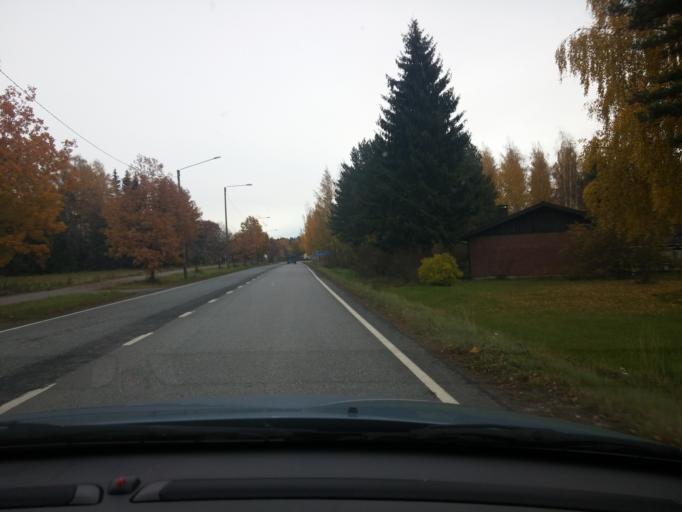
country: FI
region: Haeme
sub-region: Forssa
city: Tammela
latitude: 60.8066
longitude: 23.7896
